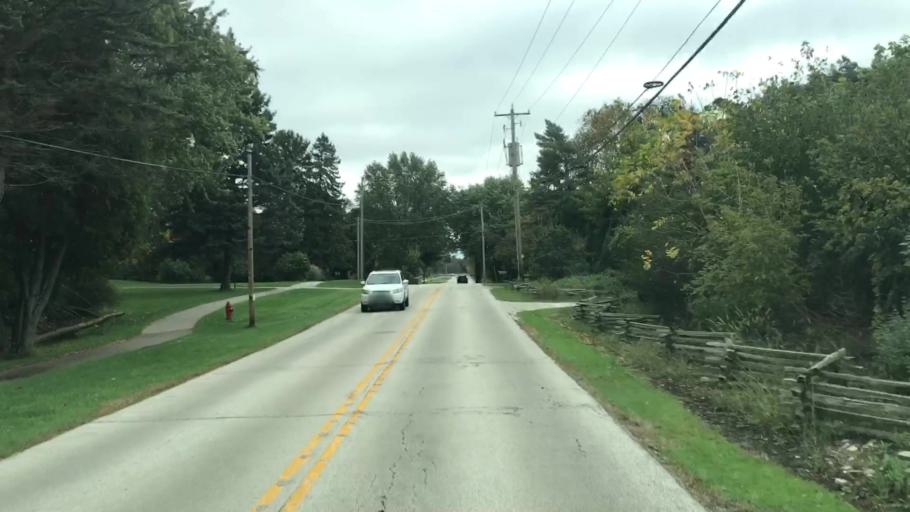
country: US
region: Wisconsin
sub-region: Waukesha County
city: Brookfield
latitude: 43.0758
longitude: -88.1350
